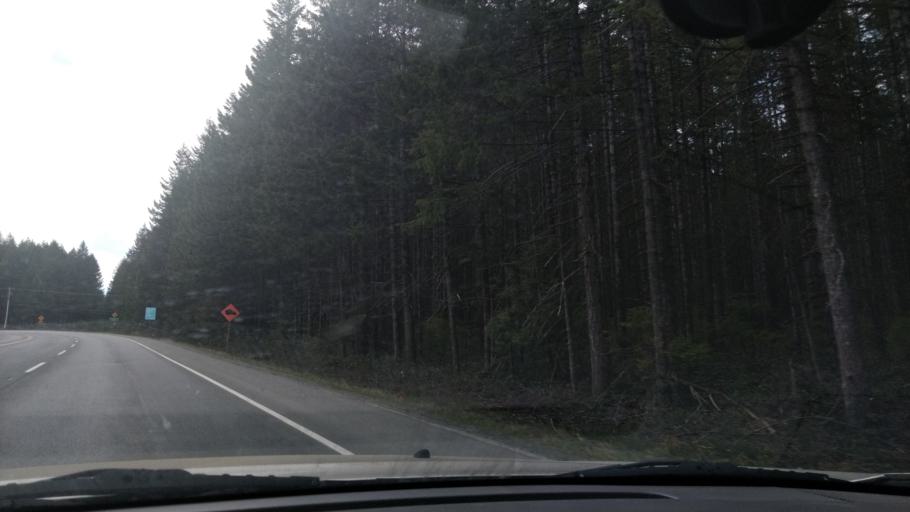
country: CA
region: British Columbia
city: Campbell River
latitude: 50.0364
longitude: -125.3265
